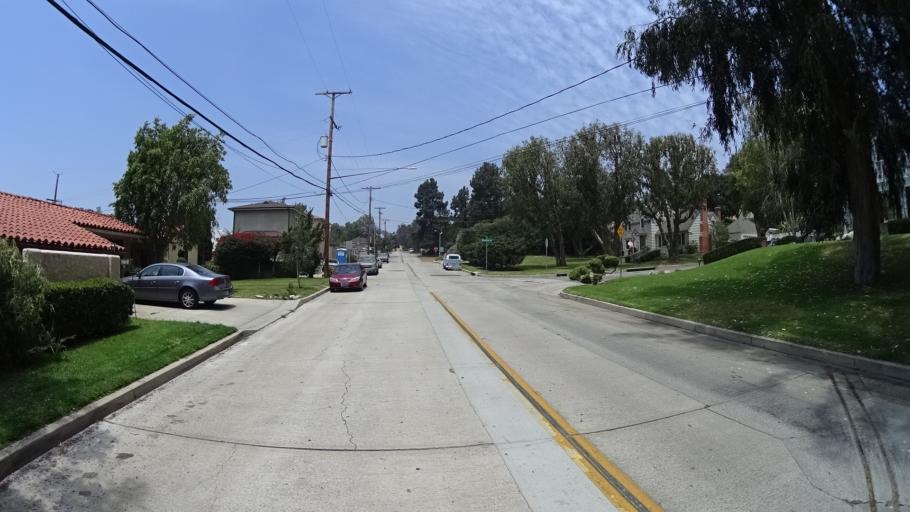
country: US
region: California
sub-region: Los Angeles County
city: Burbank
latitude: 34.1962
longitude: -118.3016
